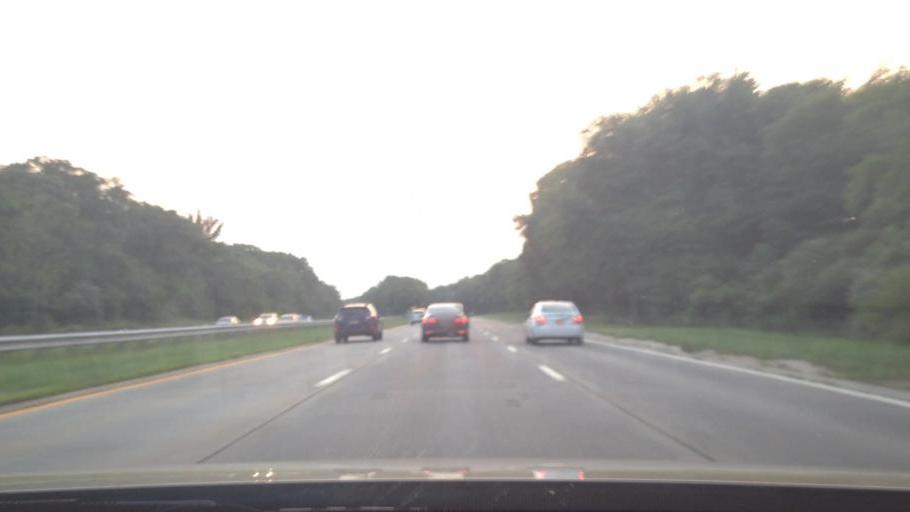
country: US
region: New York
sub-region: Suffolk County
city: Islip
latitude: 40.7547
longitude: -73.2282
